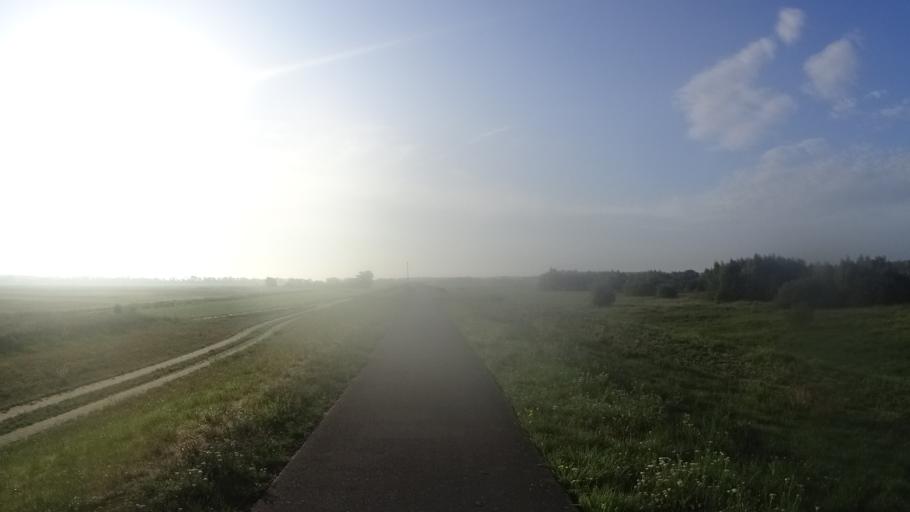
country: DE
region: Brandenburg
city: Lenzen
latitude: 53.0681
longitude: 11.4930
